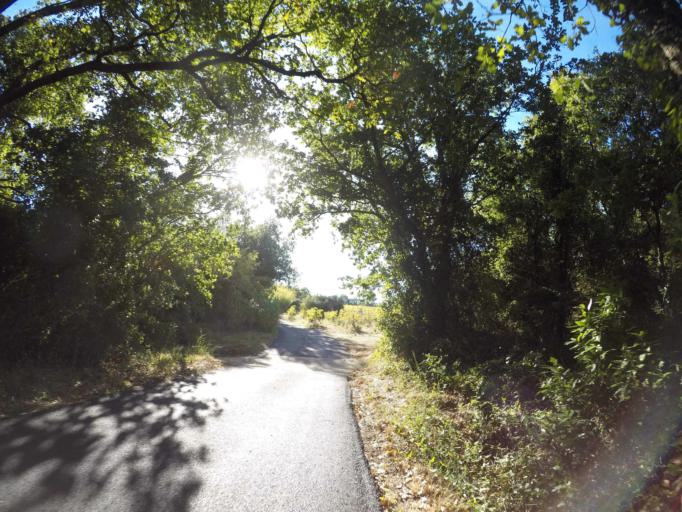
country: FR
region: Languedoc-Roussillon
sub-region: Departement des Pyrenees-Orientales
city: Trouillas
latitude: 42.5703
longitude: 2.7921
